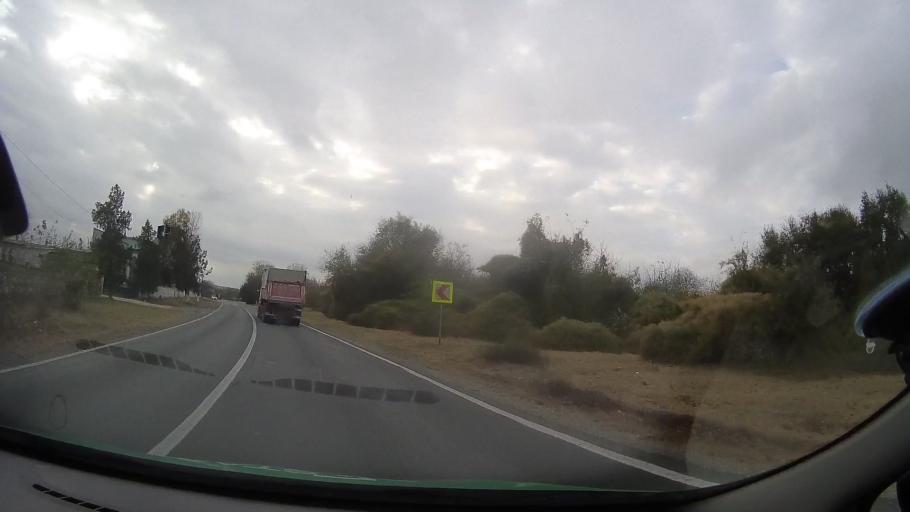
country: RO
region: Constanta
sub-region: Municipiul Medgidia
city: Medgidia
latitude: 44.2675
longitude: 28.2600
